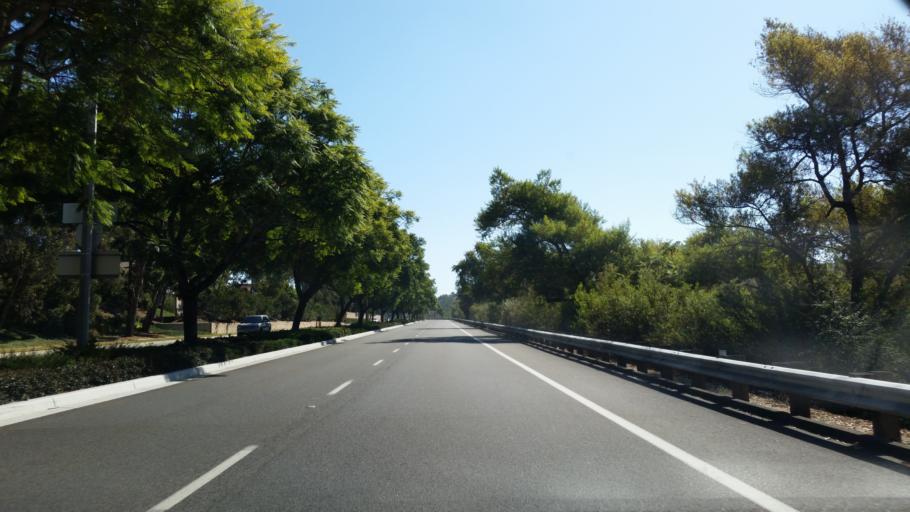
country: US
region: California
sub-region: Orange County
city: Irvine
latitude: 33.6572
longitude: -117.8257
